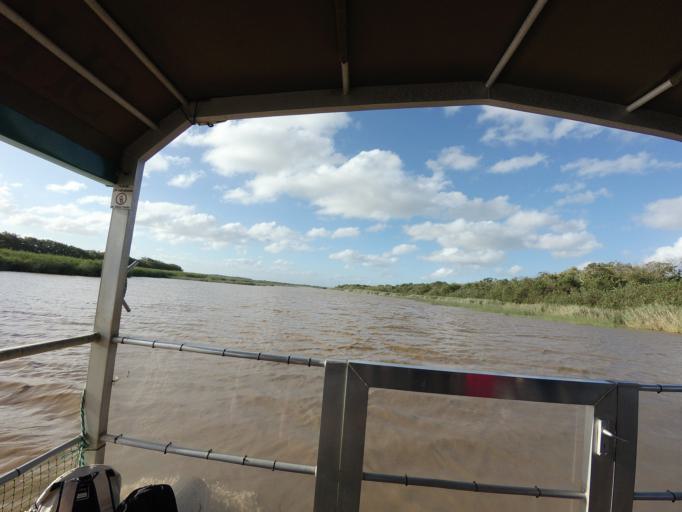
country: ZA
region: KwaZulu-Natal
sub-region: uMkhanyakude District Municipality
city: Mtubatuba
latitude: -28.3672
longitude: 32.4105
